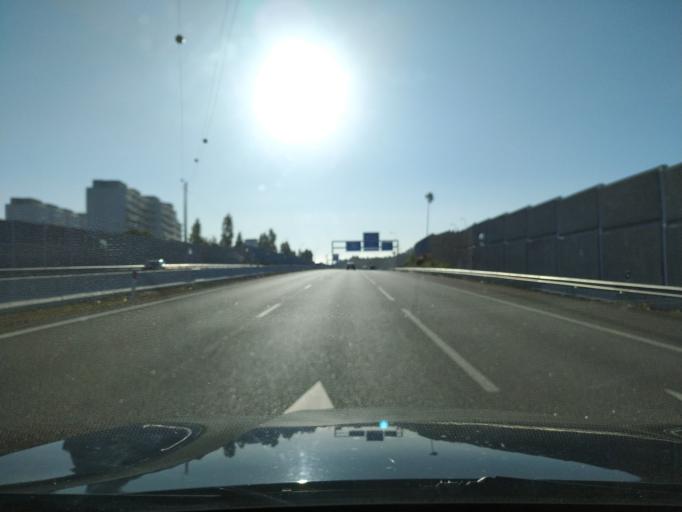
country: PT
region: Porto
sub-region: Vila Nova de Gaia
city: Vilar de Andorinho
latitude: 41.0985
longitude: -8.5946
